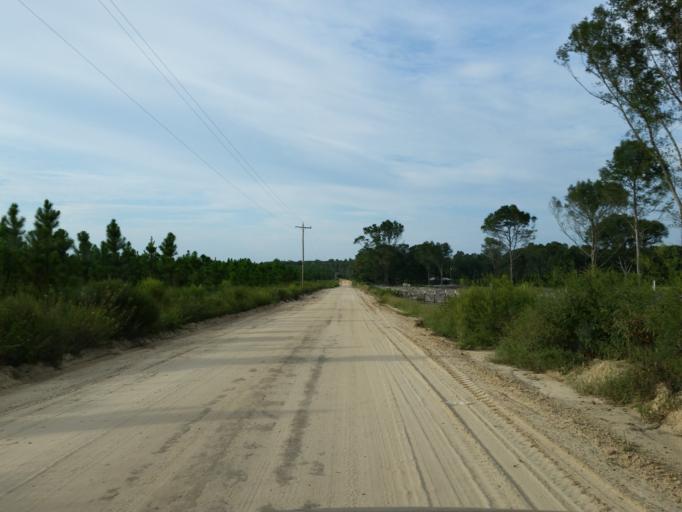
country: US
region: Florida
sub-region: Madison County
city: Madison
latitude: 30.5342
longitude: -83.2158
